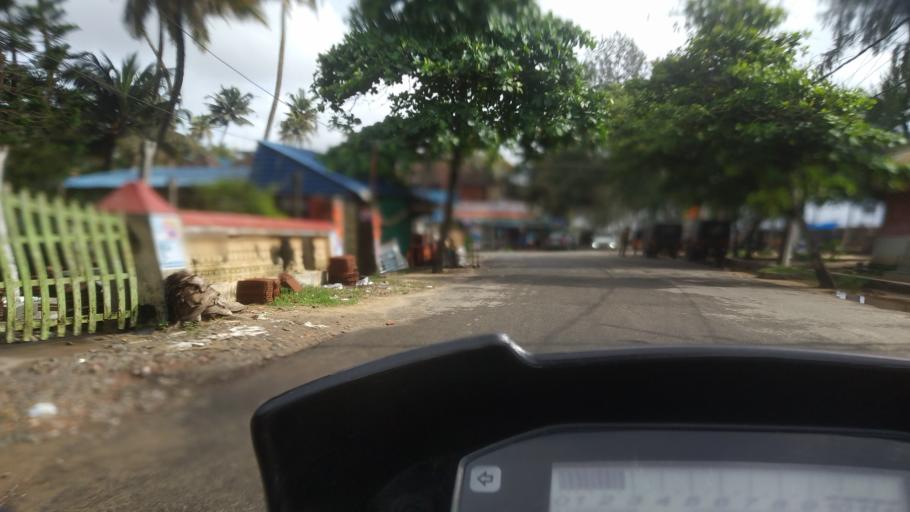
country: IN
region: Kerala
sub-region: Thrissur District
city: Kodungallur
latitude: 10.1396
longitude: 76.1793
